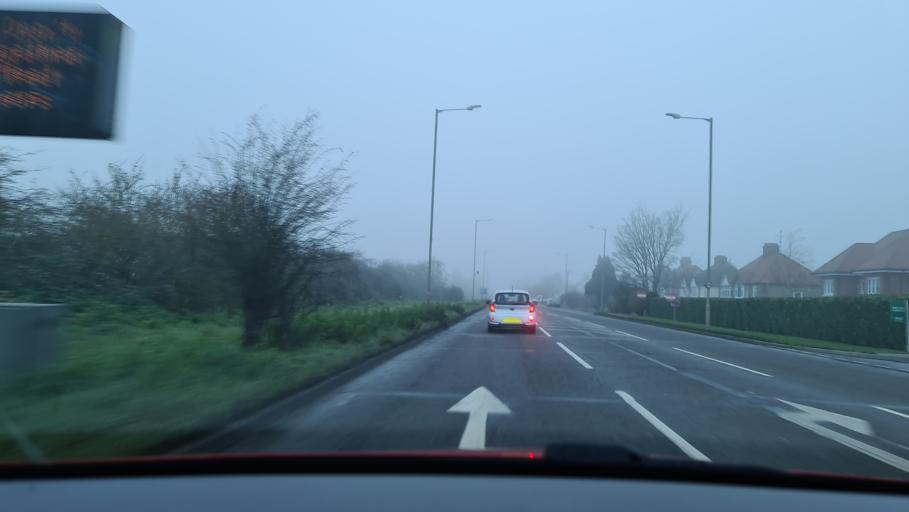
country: GB
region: England
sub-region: Buckinghamshire
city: Weston Turville
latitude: 51.8078
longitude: -0.7590
